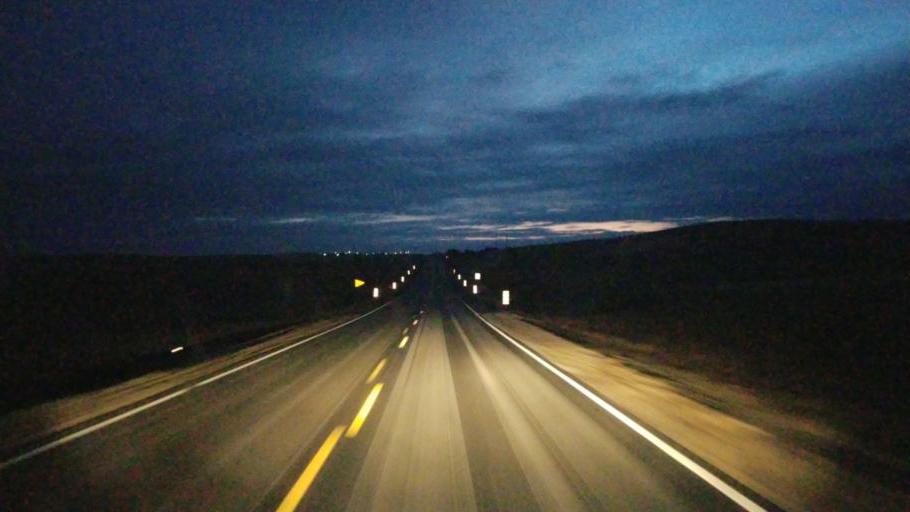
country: US
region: Nebraska
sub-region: Knox County
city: Center
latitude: 42.5972
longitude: -97.8299
